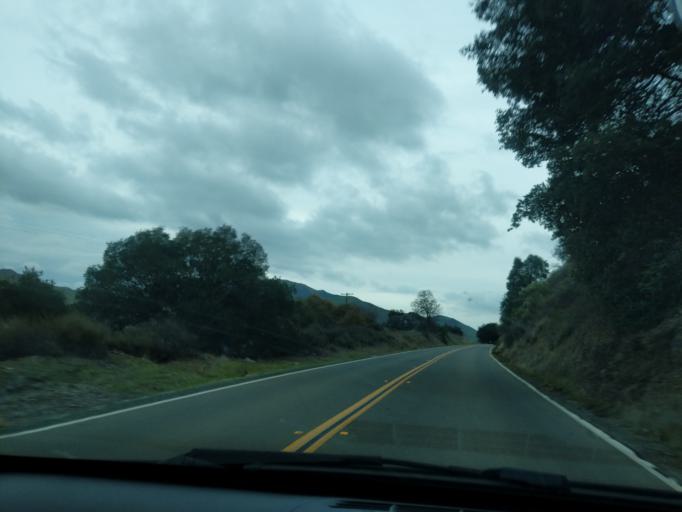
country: US
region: California
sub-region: Monterey County
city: Soledad
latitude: 36.6058
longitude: -121.1990
